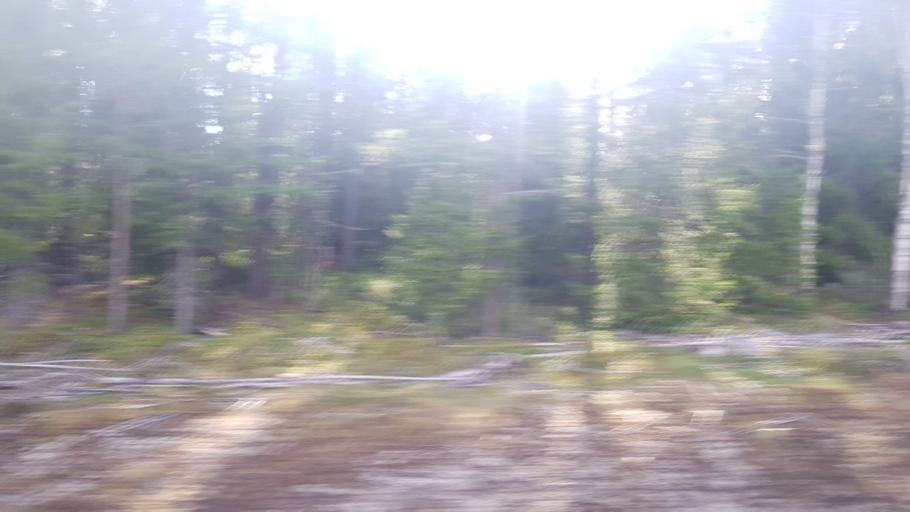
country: NO
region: Sor-Trondelag
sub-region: Rennebu
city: Berkak
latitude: 62.9065
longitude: 10.1236
